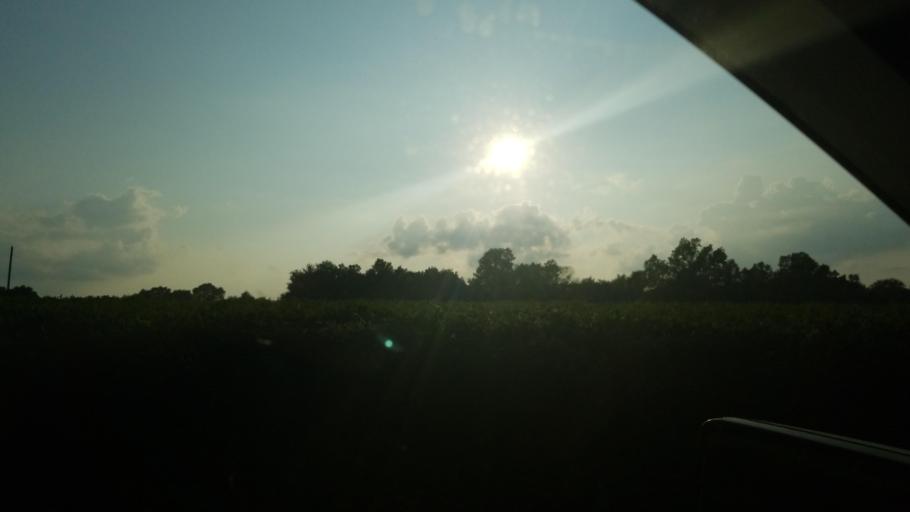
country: US
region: Illinois
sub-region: Saline County
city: Harrisburg
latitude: 37.8127
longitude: -88.6146
